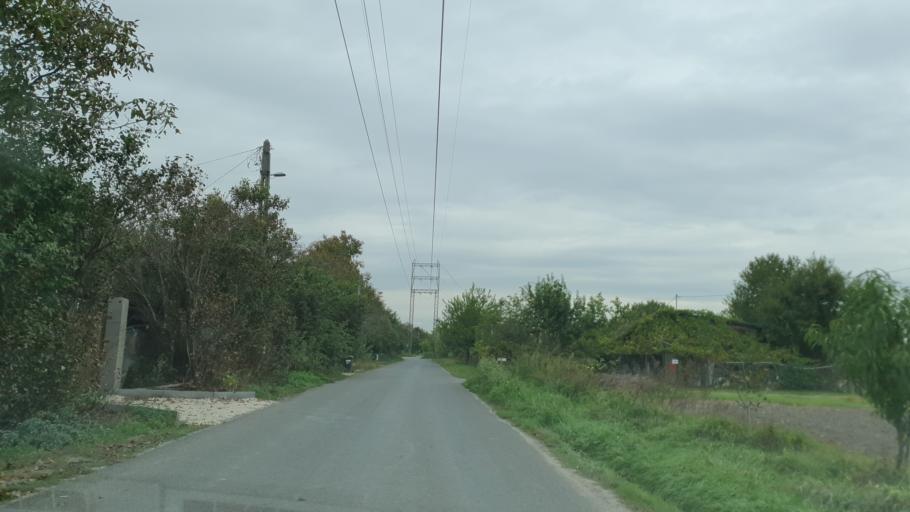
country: HU
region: Pest
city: Dunaharaszti
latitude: 47.3819
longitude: 19.0795
